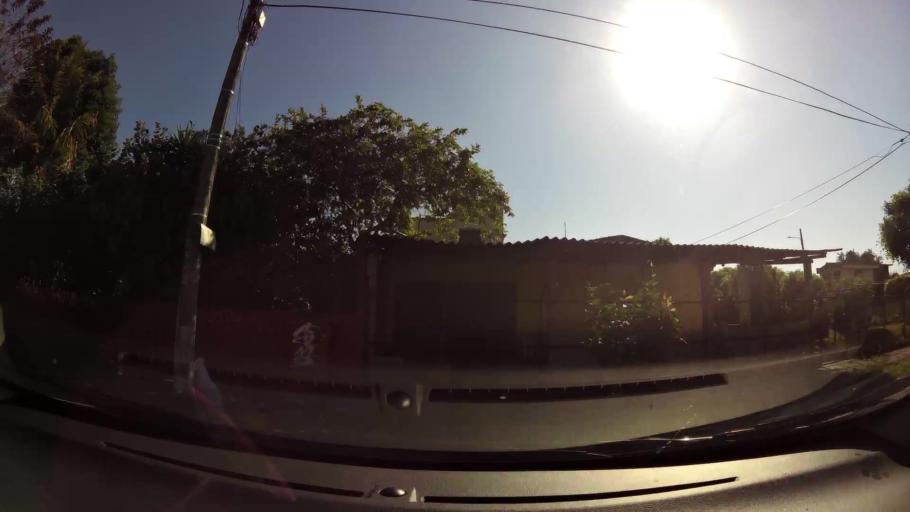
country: SV
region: La Libertad
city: Santa Tecla
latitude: 13.6786
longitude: -89.2924
